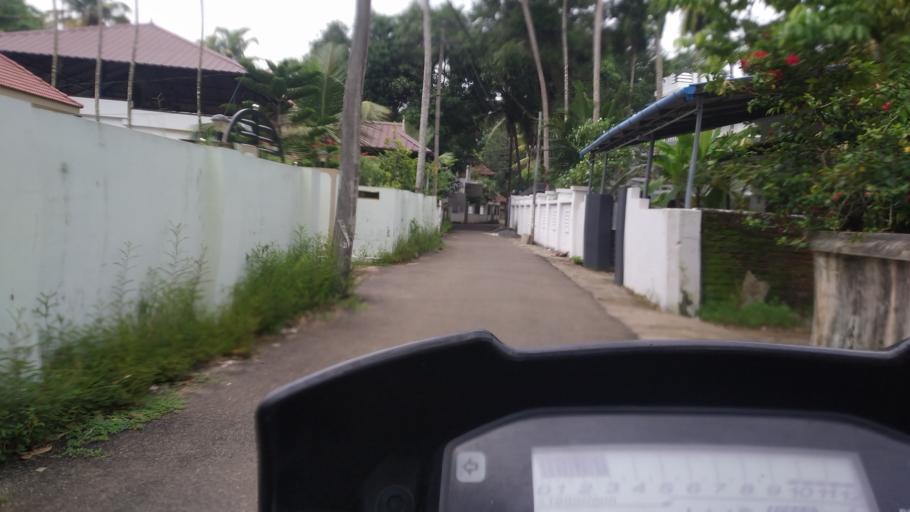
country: IN
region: Kerala
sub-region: Ernakulam
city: Elur
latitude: 10.0593
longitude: 76.2182
